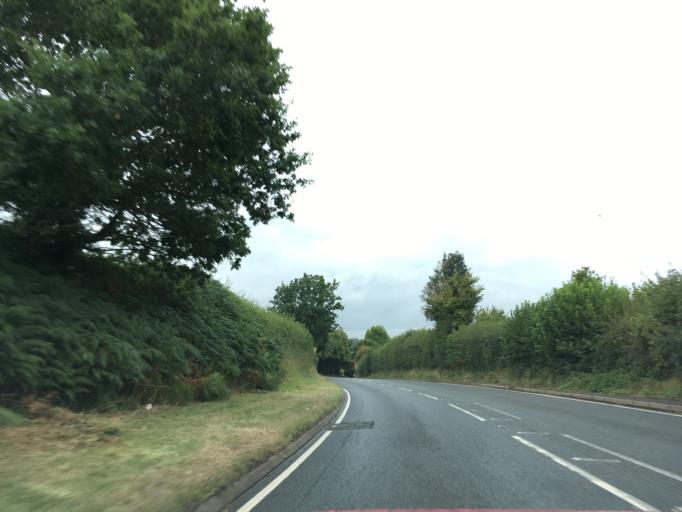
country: GB
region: England
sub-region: Herefordshire
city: Lea
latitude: 51.8978
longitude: -2.5200
